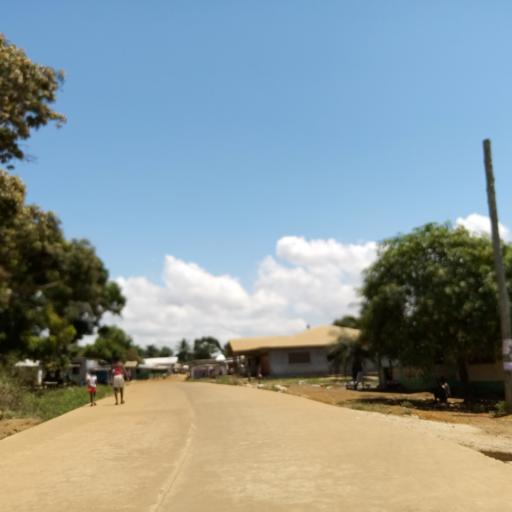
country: LR
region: Montserrado
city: Monrovia
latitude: 6.2480
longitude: -10.6906
